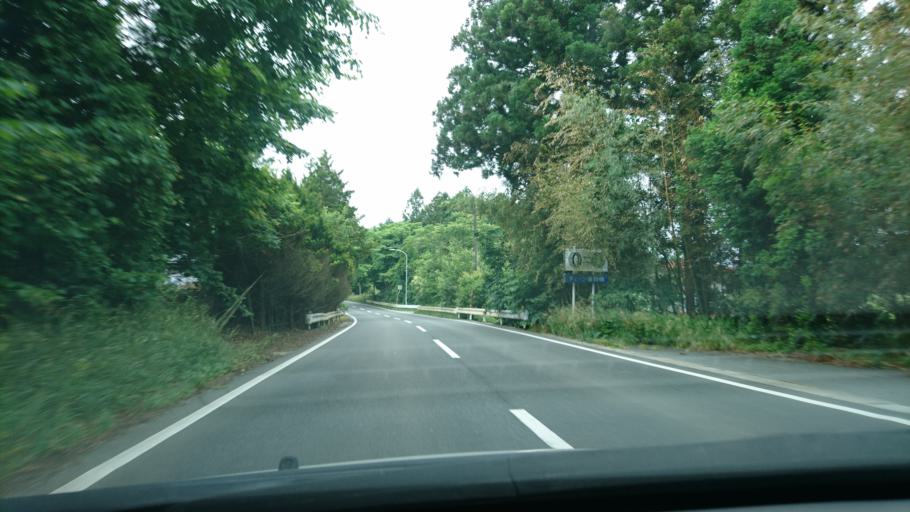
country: JP
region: Iwate
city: Ichinoseki
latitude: 38.7594
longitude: 141.2571
